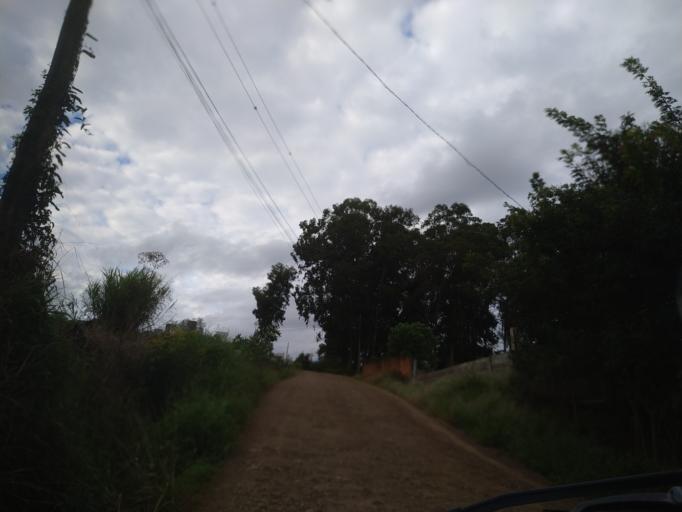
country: BR
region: Santa Catarina
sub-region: Chapeco
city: Chapeco
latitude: -27.0675
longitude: -52.6121
